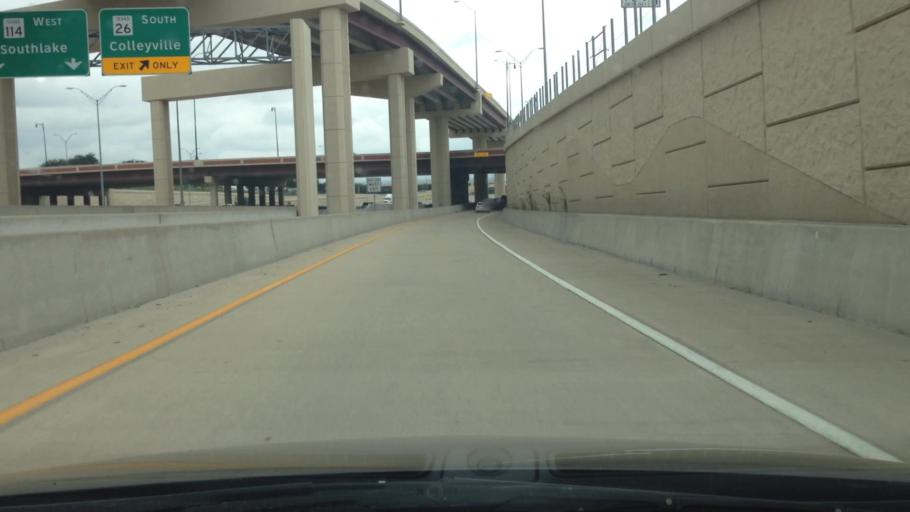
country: US
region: Texas
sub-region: Tarrant County
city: Grapevine
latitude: 32.9248
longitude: -97.0867
